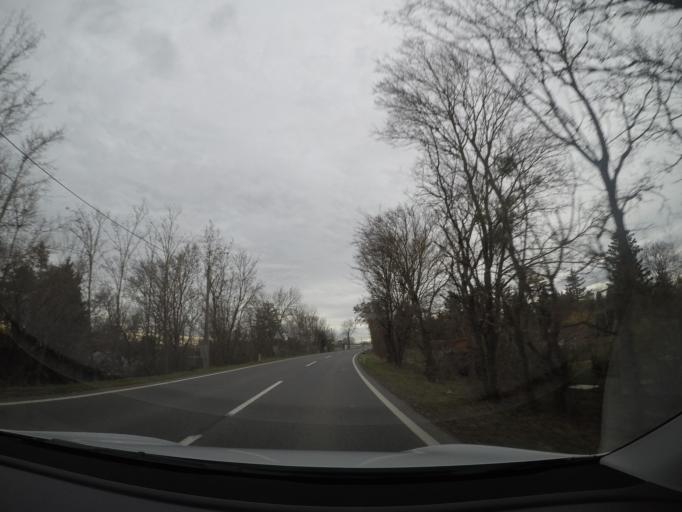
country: AT
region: Lower Austria
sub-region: Politischer Bezirk Modling
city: Achau
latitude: 48.0799
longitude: 16.3911
